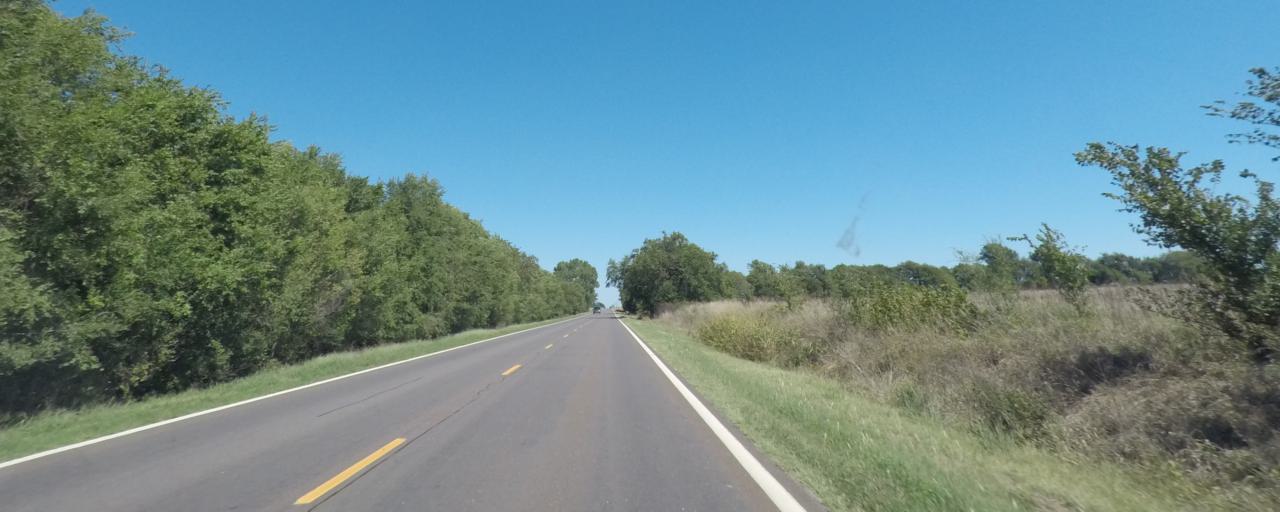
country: US
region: Kansas
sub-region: Sumner County
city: Wellington
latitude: 37.0769
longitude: -97.4014
